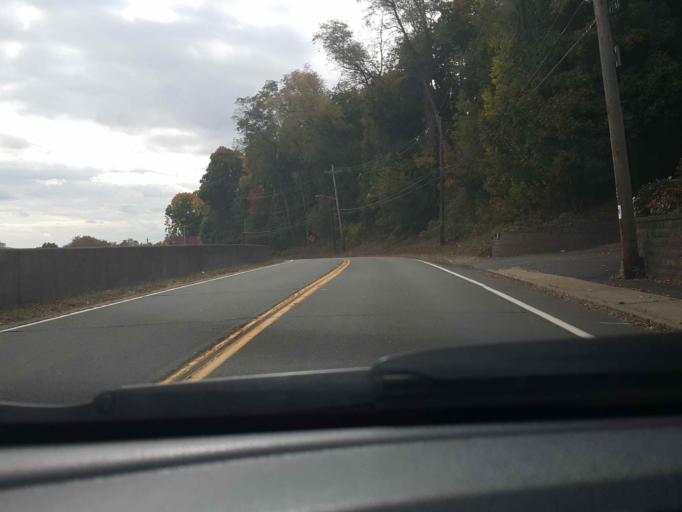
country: US
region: New York
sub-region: Rockland County
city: South Nyack
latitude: 41.0819
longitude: -73.9241
